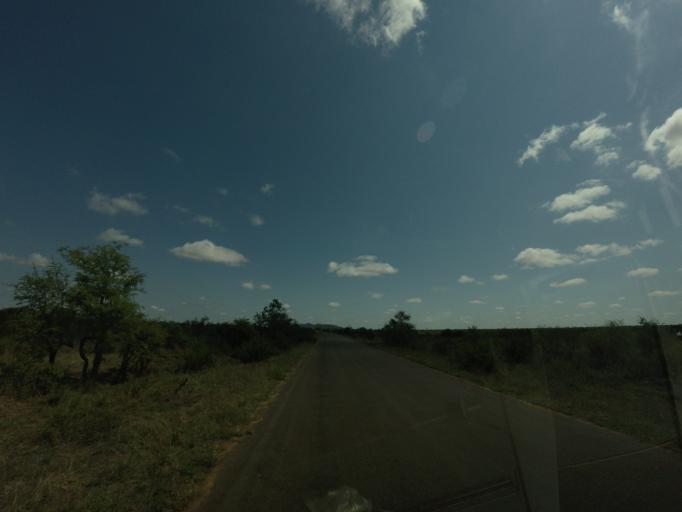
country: ZA
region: Mpumalanga
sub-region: Ehlanzeni District
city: Komatipoort
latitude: -25.0845
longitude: 31.9189
